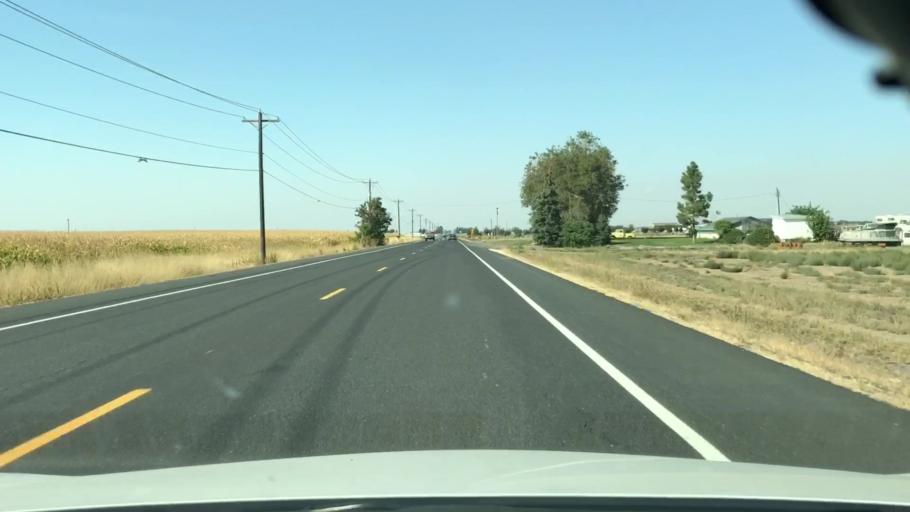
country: US
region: Washington
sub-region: Grant County
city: Moses Lake
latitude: 47.1205
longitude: -119.2358
